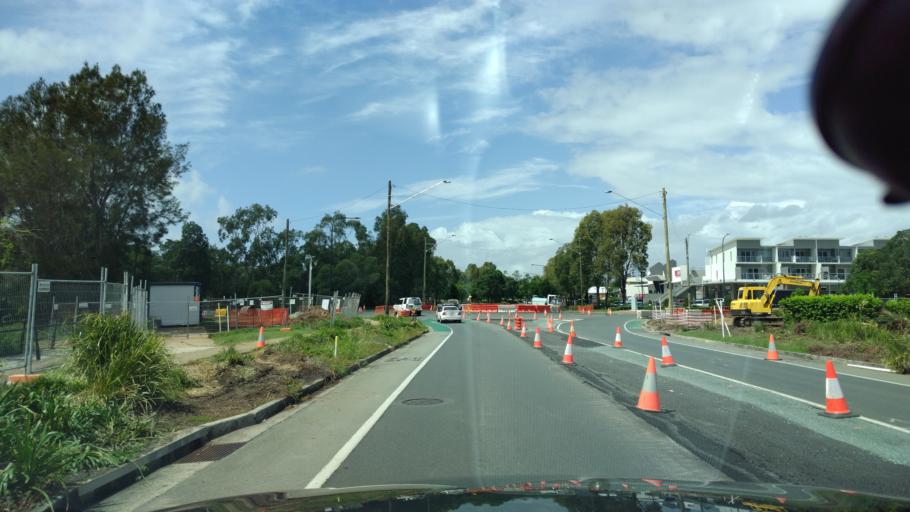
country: AU
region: Queensland
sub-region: Moreton Bay
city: Mango Hill
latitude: -27.2358
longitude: 153.0217
